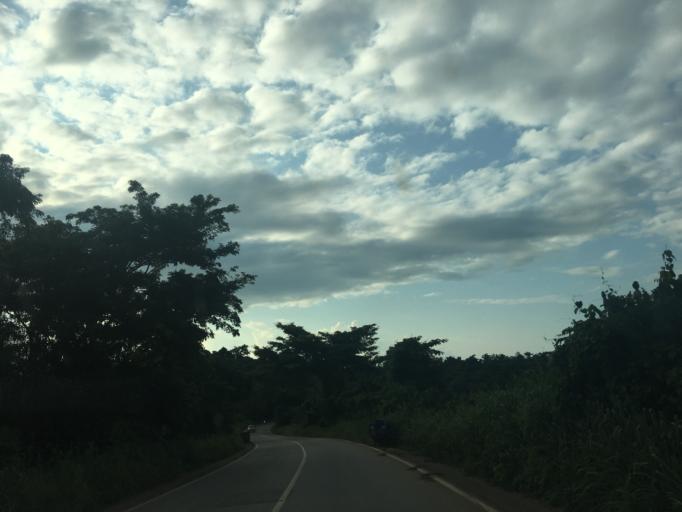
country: GH
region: Western
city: Bibiani
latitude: 6.4112
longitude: -2.3014
